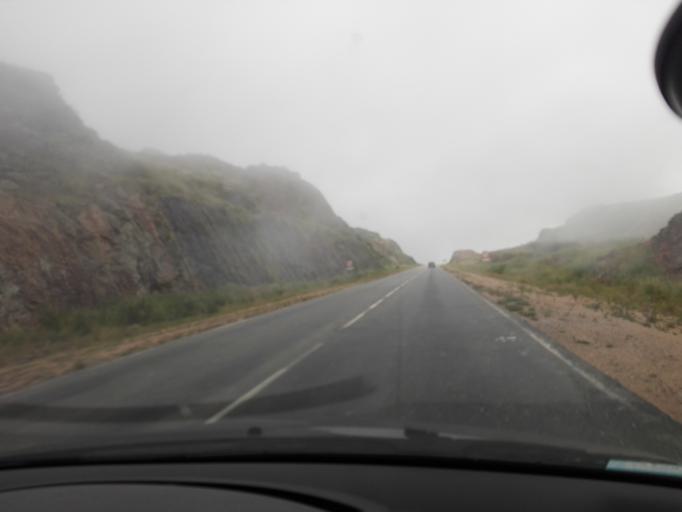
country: AR
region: Cordoba
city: Cuesta Blanca
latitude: -31.6156
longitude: -64.7415
